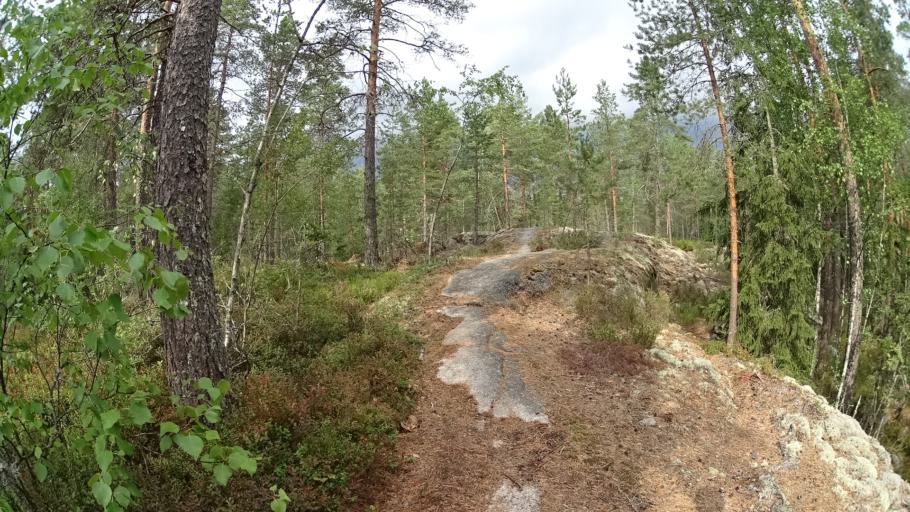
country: FI
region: Uusimaa
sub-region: Helsinki
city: Espoo
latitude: 60.3054
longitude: 24.5797
